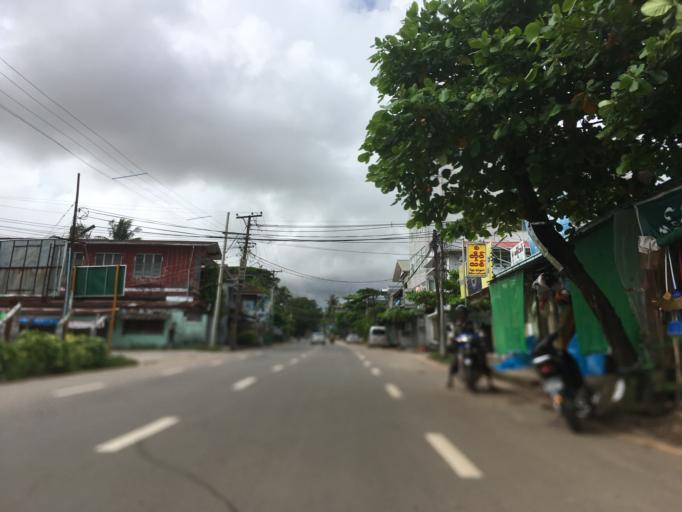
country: MM
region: Mon
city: Mawlamyine
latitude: 16.4656
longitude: 97.6238
